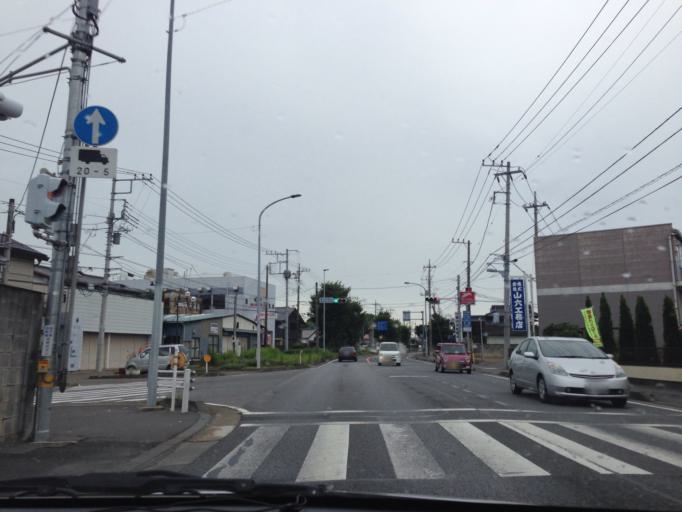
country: JP
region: Ibaraki
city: Naka
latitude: 36.0255
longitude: 140.1610
